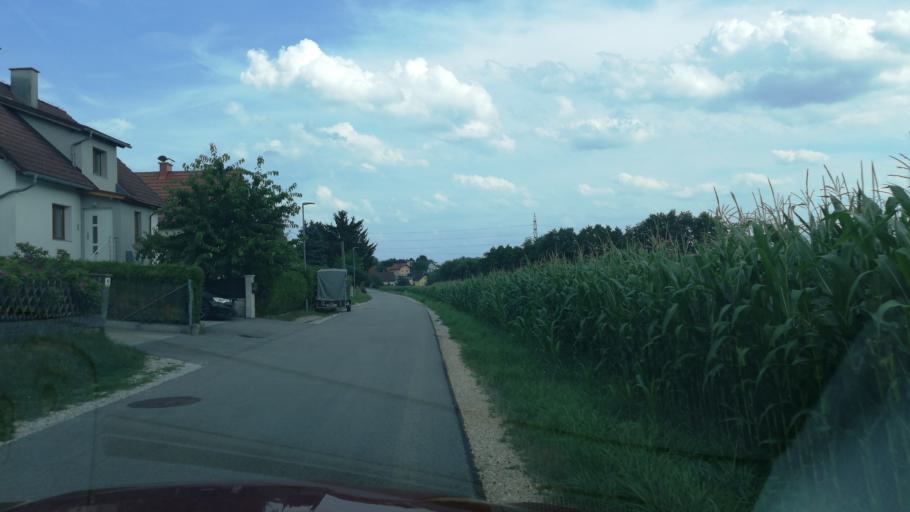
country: AT
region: Upper Austria
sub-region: Wels-Land
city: Lambach
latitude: 48.1020
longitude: 13.8576
